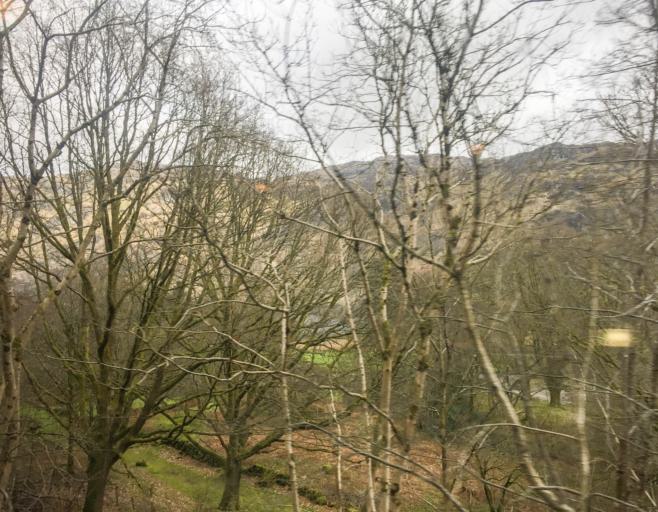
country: GB
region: Scotland
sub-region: Argyll and Bute
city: Garelochhead
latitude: 56.2712
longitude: -4.7077
